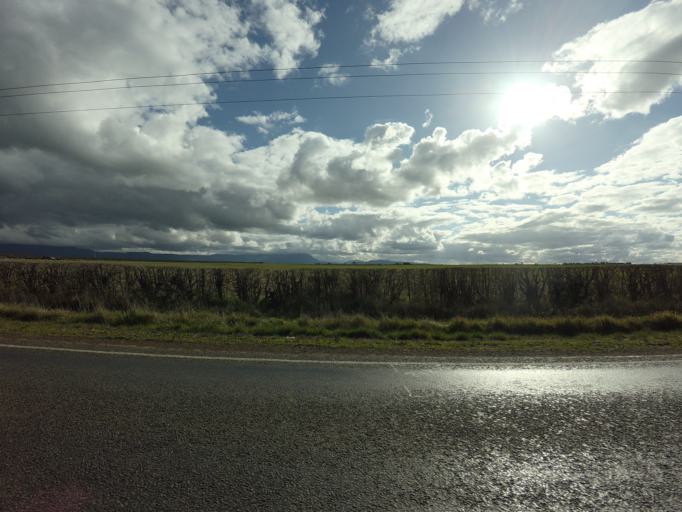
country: AU
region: Tasmania
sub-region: Northern Midlands
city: Longford
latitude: -41.7011
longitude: 147.0770
